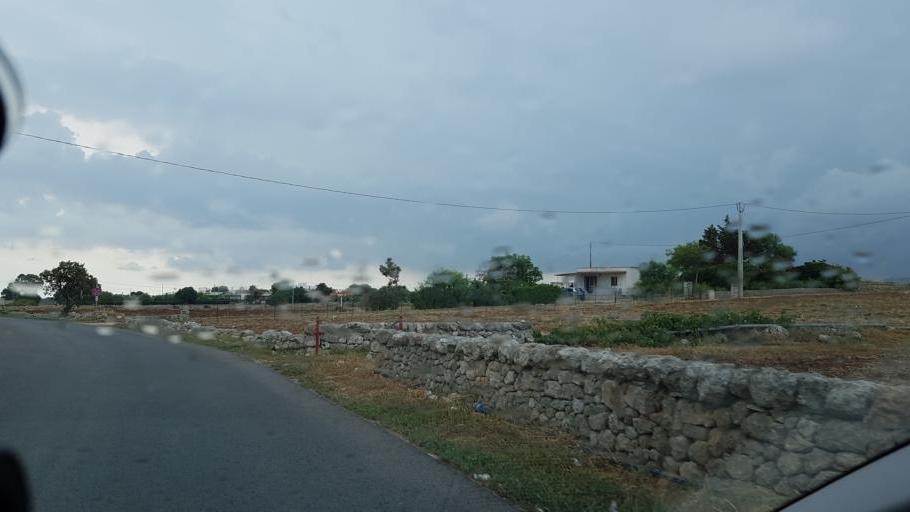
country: IT
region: Apulia
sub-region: Provincia di Bari
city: Monopoli
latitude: 40.9353
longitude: 17.3202
